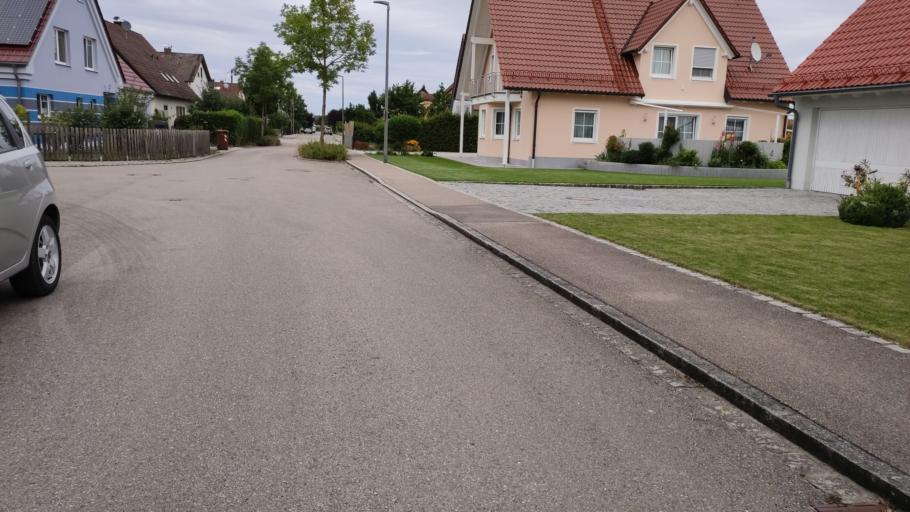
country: DE
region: Bavaria
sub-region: Swabia
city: Oberottmarshausen
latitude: 48.2334
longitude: 10.8599
